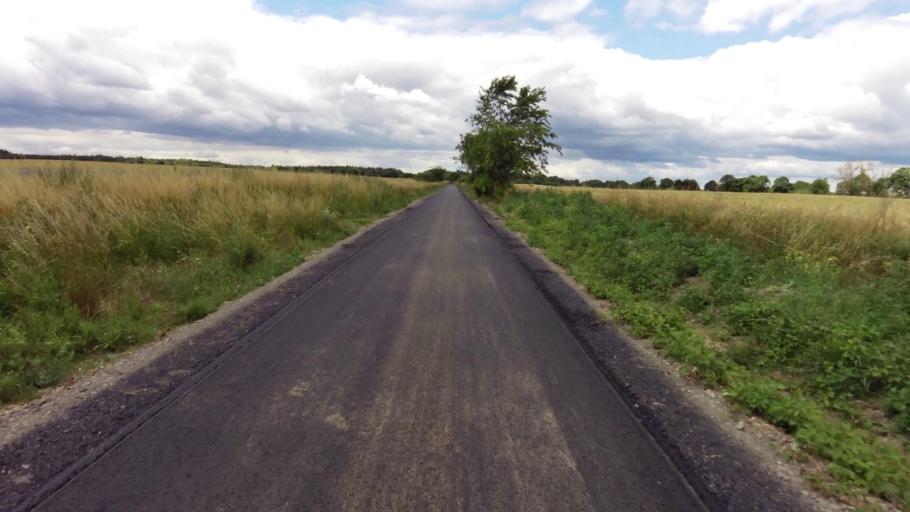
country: PL
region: West Pomeranian Voivodeship
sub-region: Powiat mysliborski
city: Barlinek
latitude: 52.9875
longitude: 15.1434
